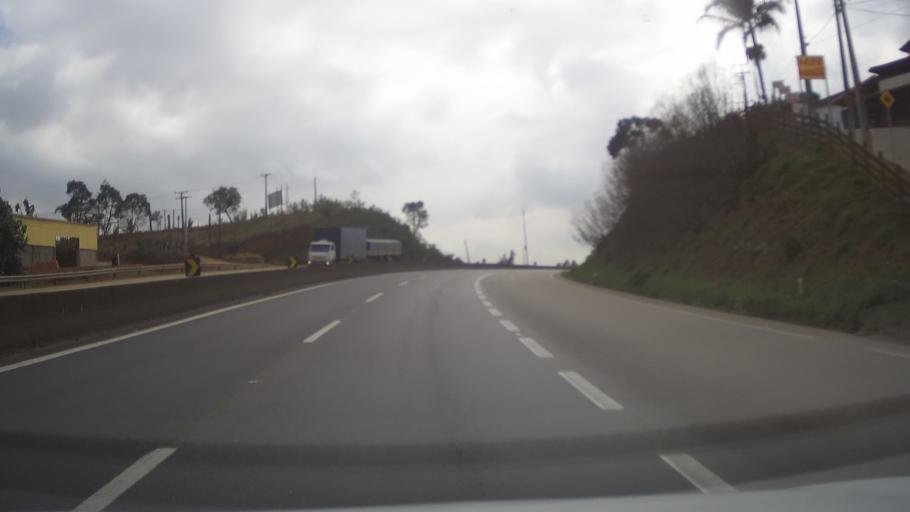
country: BR
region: Minas Gerais
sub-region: Extrema
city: Extrema
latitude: -22.8239
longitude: -46.3087
